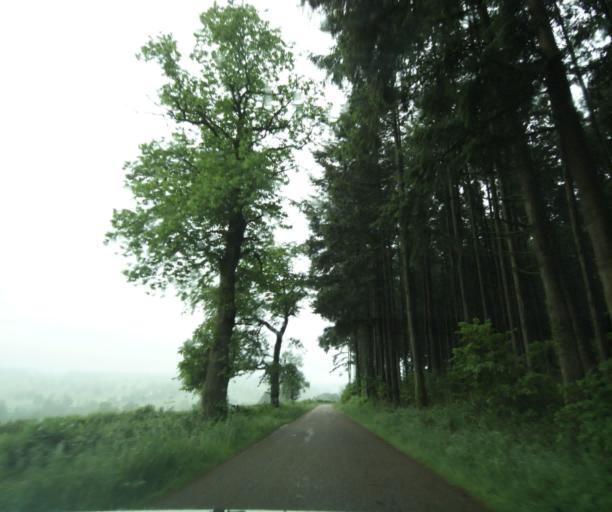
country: FR
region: Bourgogne
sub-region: Departement de Saone-et-Loire
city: Charolles
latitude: 46.3837
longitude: 4.3404
